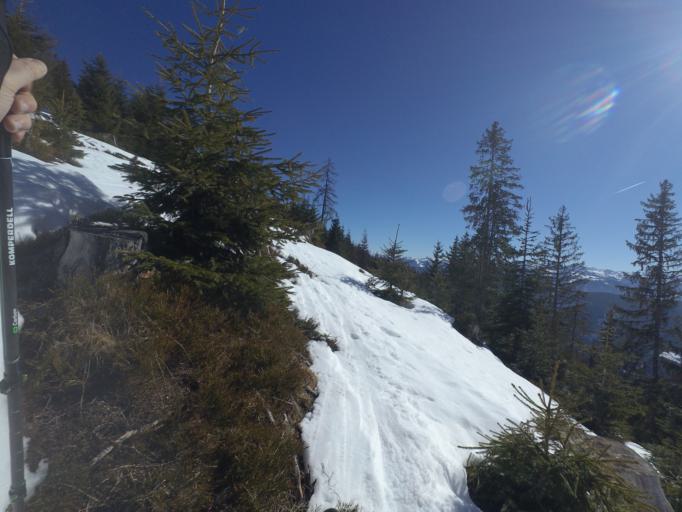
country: AT
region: Salzburg
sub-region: Politischer Bezirk Sankt Johann im Pongau
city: Muhlbach am Hochkonig
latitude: 47.3957
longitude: 13.1267
